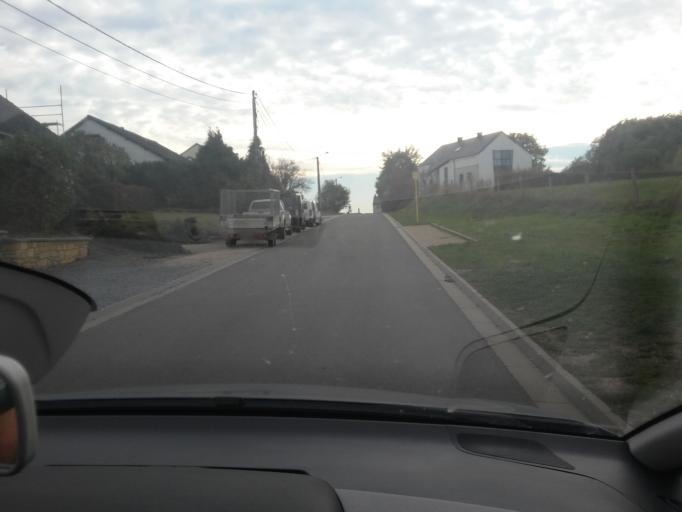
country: BE
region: Wallonia
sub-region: Province du Luxembourg
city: Attert
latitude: 49.7478
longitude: 5.7672
